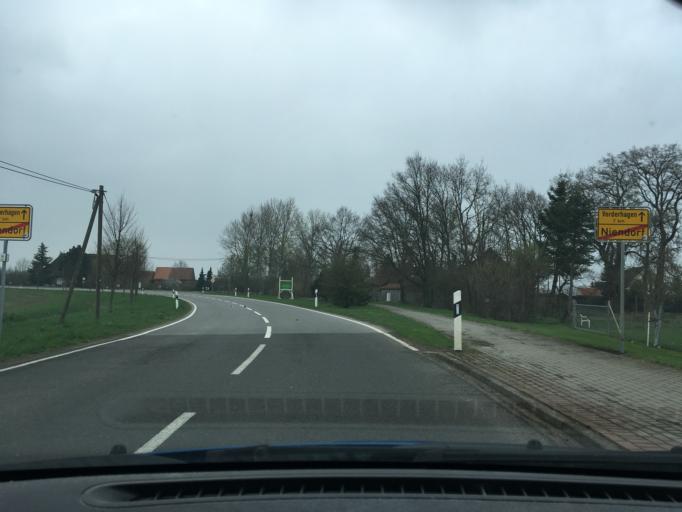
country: DE
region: Lower Saxony
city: Neu Darchau
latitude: 53.3107
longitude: 10.8914
